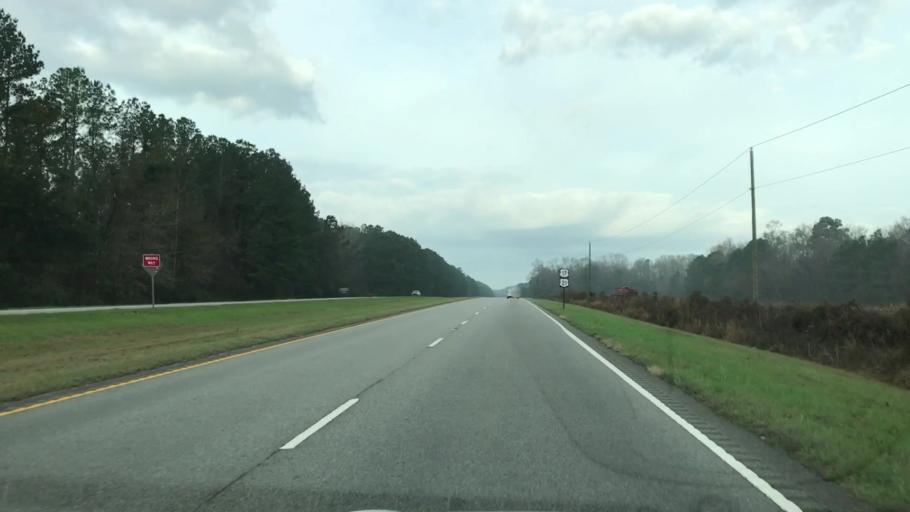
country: US
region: South Carolina
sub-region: Hampton County
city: Yemassee
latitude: 32.6125
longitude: -80.8128
